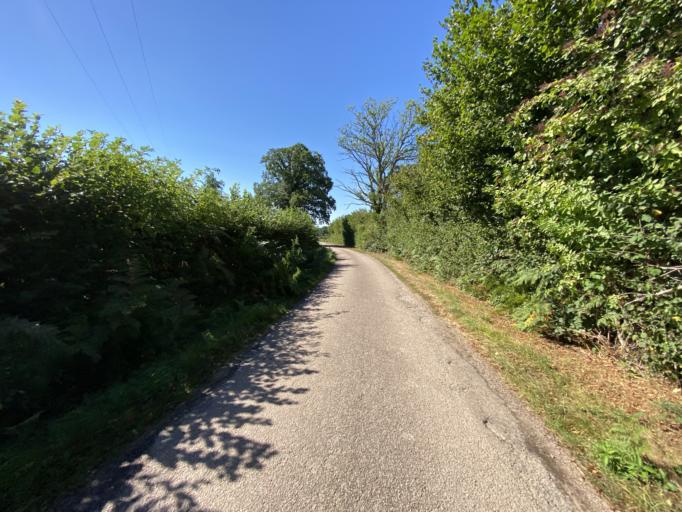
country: FR
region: Bourgogne
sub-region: Departement de la Cote-d'Or
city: Saulieu
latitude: 47.2797
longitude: 4.1796
